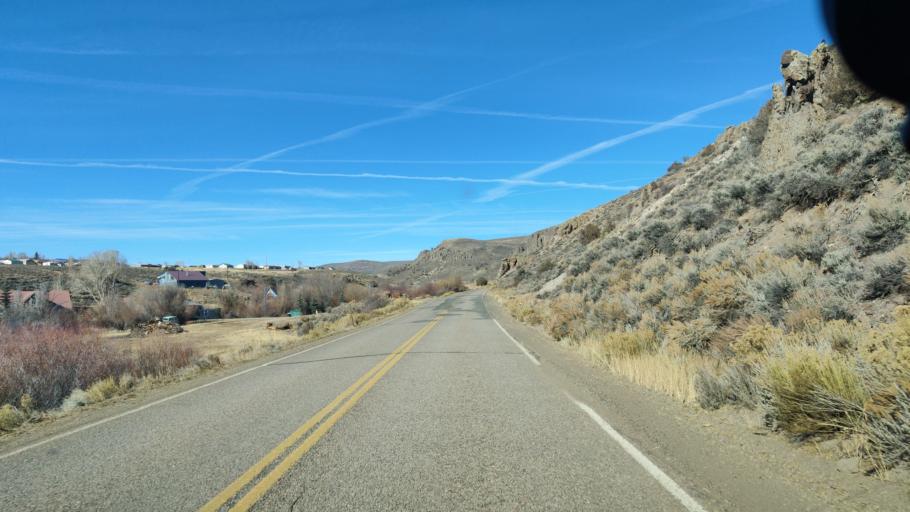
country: US
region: Colorado
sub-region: Gunnison County
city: Gunnison
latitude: 38.5707
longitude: -106.9606
